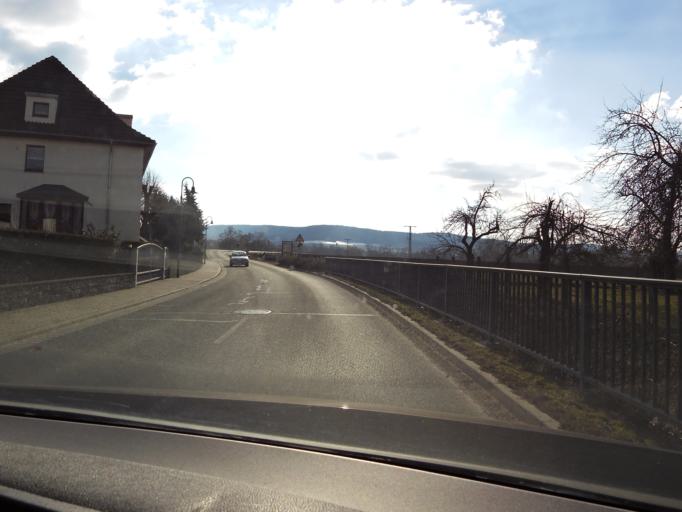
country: DE
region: Thuringia
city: Leimbach
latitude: 50.8292
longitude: 10.1929
